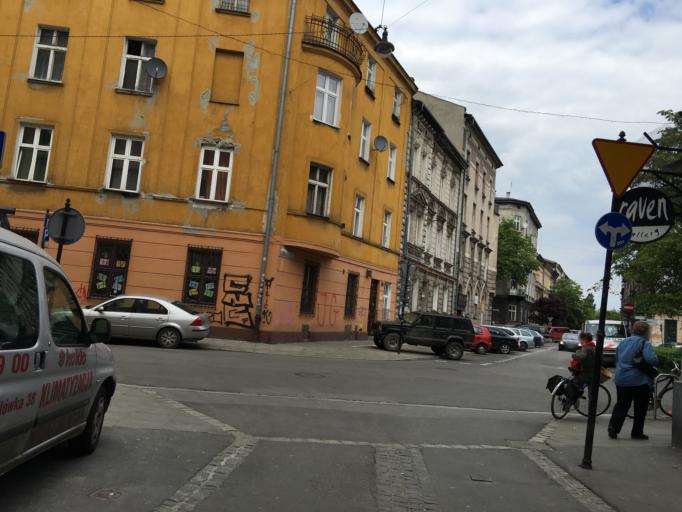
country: PL
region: Lesser Poland Voivodeship
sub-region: Krakow
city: Krakow
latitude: 50.0536
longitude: 19.9450
